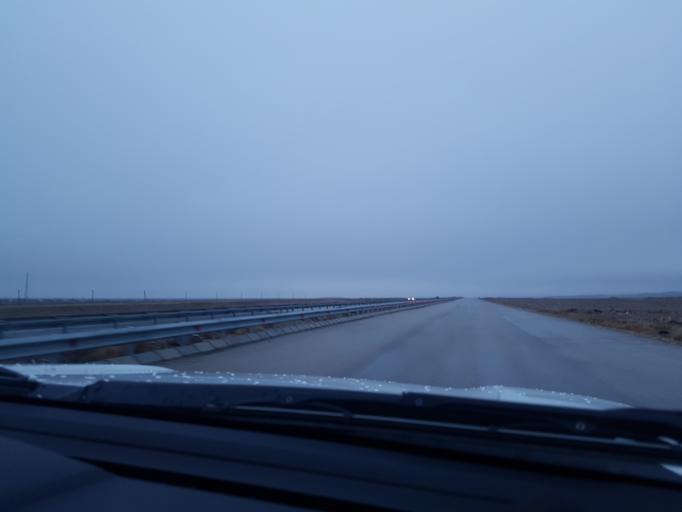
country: TM
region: Balkan
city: Balkanabat
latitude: 39.8884
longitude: 54.0366
